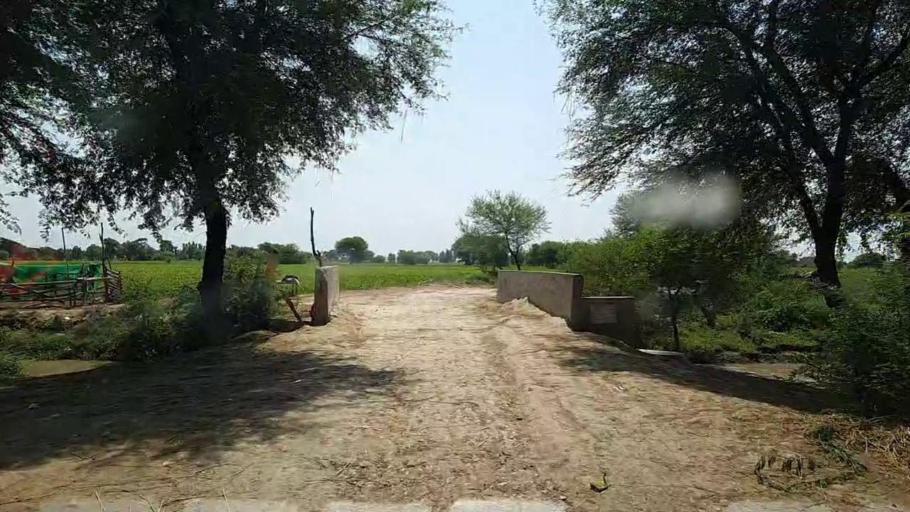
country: PK
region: Sindh
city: Kario
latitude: 24.6449
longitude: 68.4863
